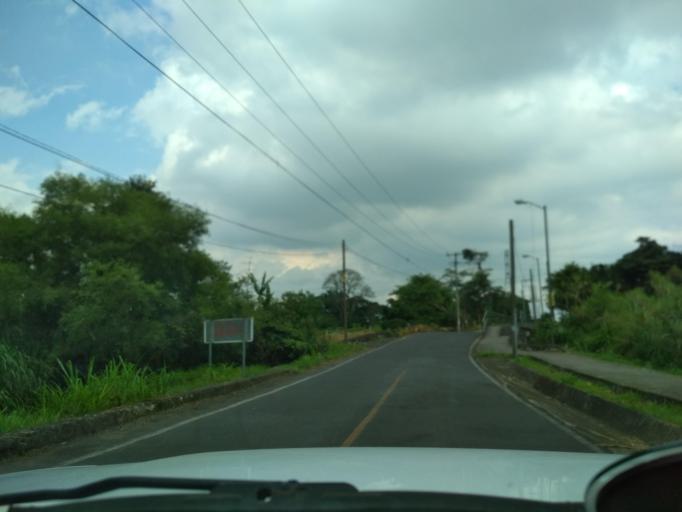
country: MX
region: Veracruz
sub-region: Ixtaczoquitlan
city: Buenavista
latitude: 18.9132
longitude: -97.0261
